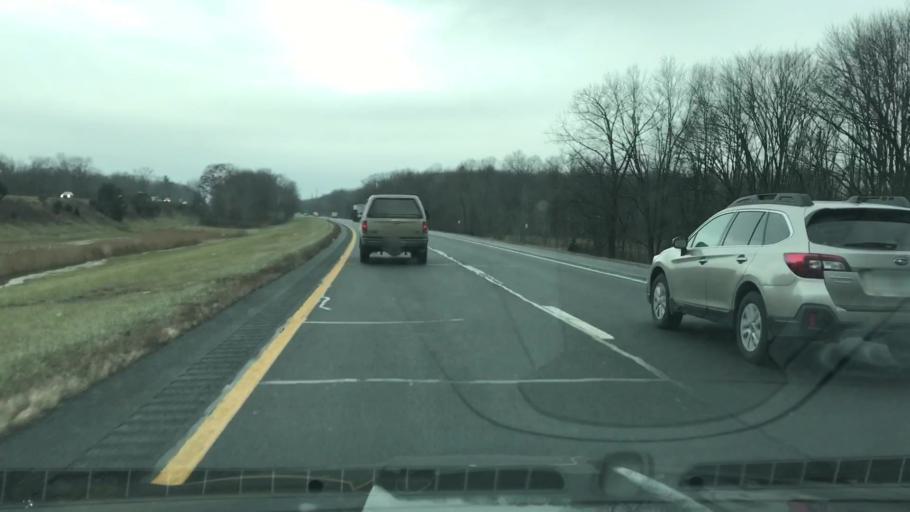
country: US
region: New York
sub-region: Orange County
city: Walden
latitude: 41.5169
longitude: -74.1691
